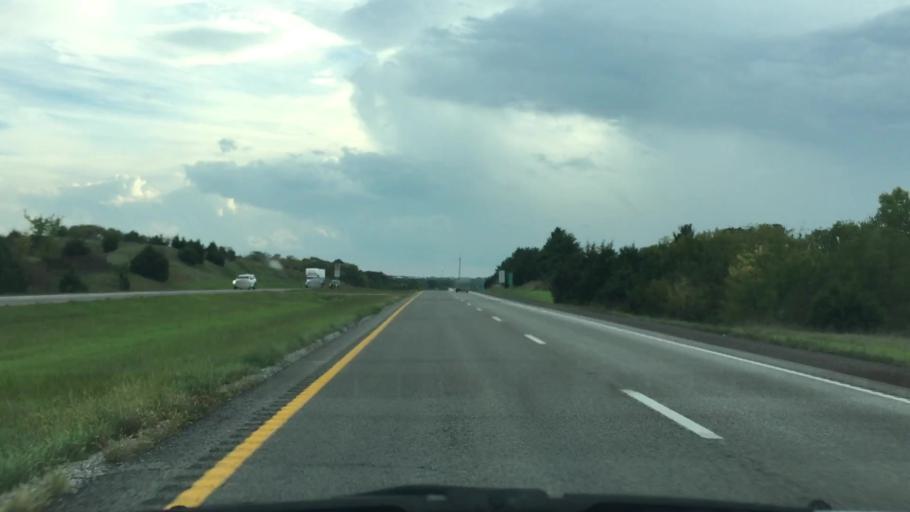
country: US
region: Missouri
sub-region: Clinton County
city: Cameron
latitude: 39.8932
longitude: -94.1550
